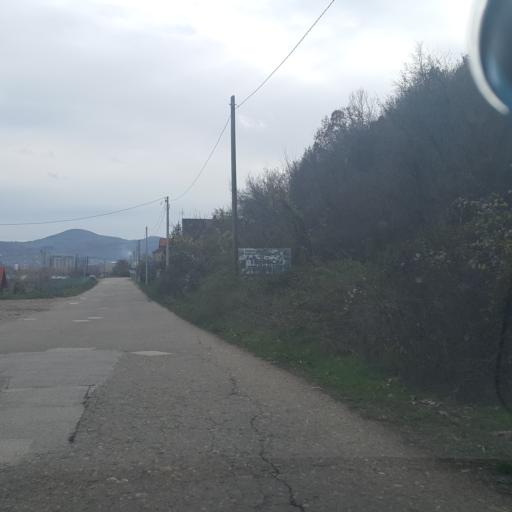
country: RS
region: Central Serbia
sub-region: Zajecarski Okrug
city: Knjazevac
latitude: 43.5792
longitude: 22.2475
